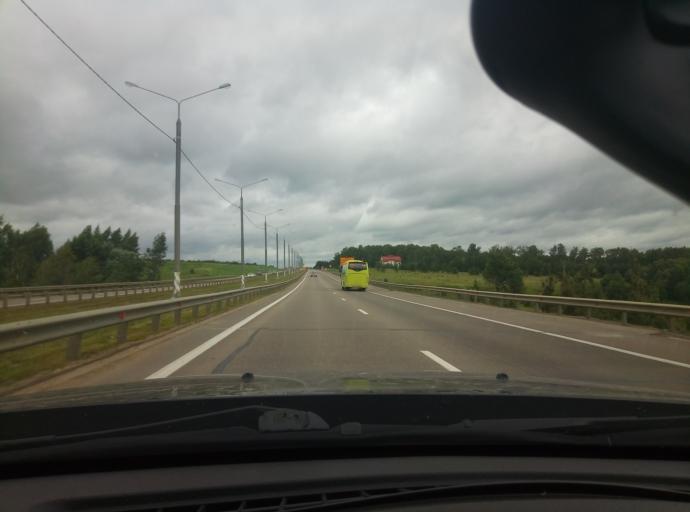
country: RU
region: Tula
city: Zaokskiy
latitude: 54.6948
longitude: 37.5100
